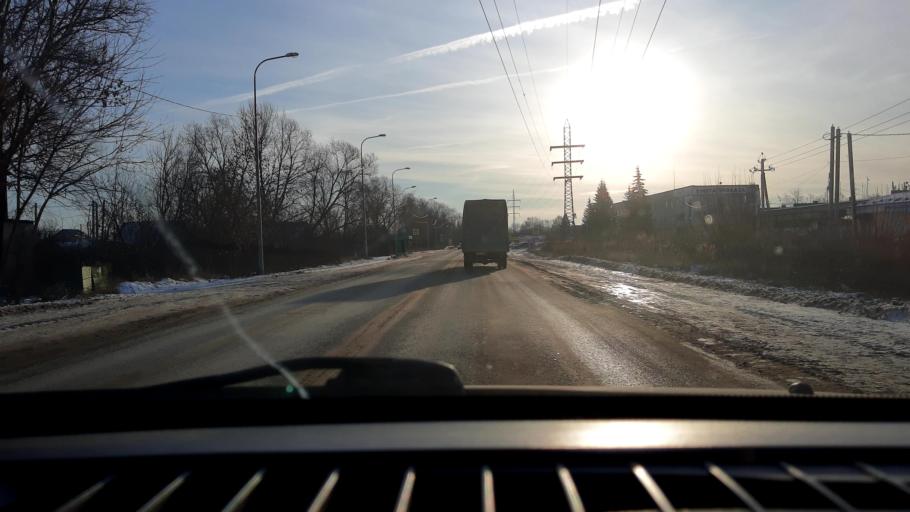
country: RU
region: Nizjnij Novgorod
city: Bor
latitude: 56.3708
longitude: 44.0659
